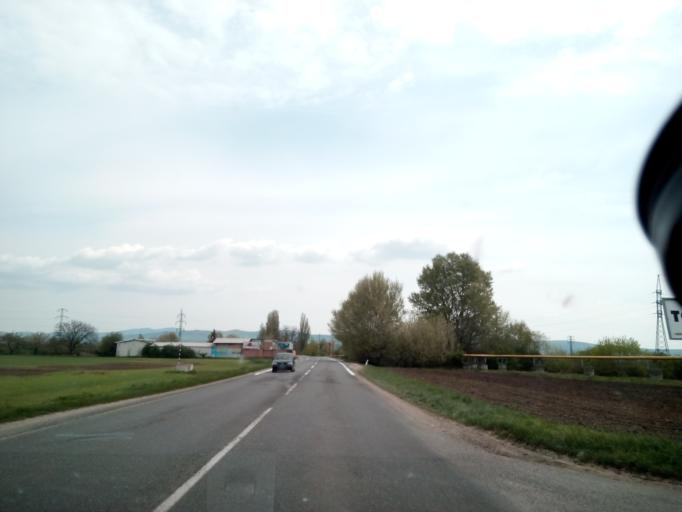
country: SK
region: Trnavsky
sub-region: Okres Trnava
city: Piestany
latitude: 48.5897
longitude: 17.7791
